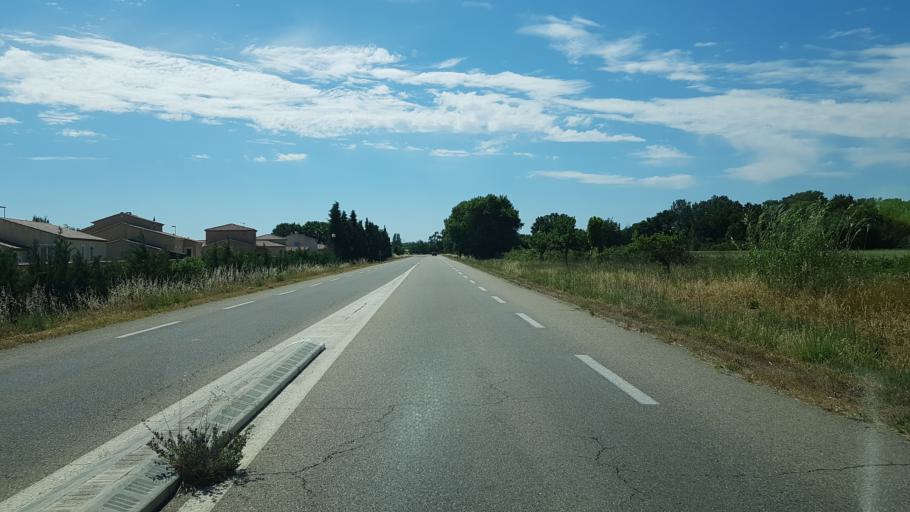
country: FR
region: Provence-Alpes-Cote d'Azur
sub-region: Departement des Bouches-du-Rhone
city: Saint-Martin-de-Crau
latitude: 43.6463
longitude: 4.8160
